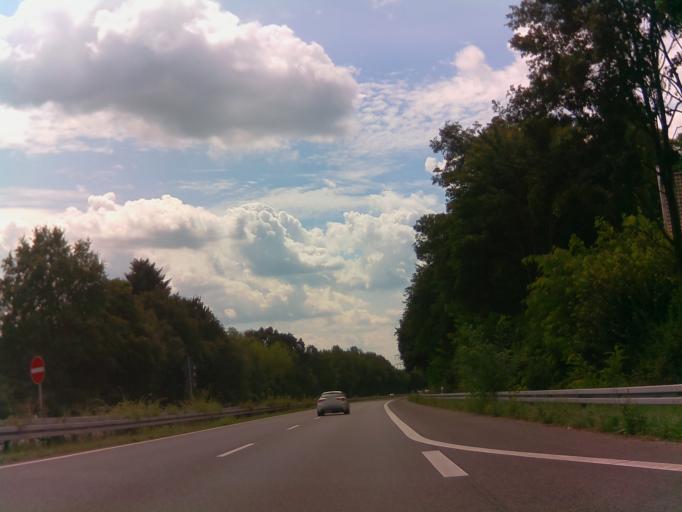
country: DE
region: Hesse
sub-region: Regierungsbezirk Darmstadt
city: Hanau am Main
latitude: 50.1037
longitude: 8.8991
